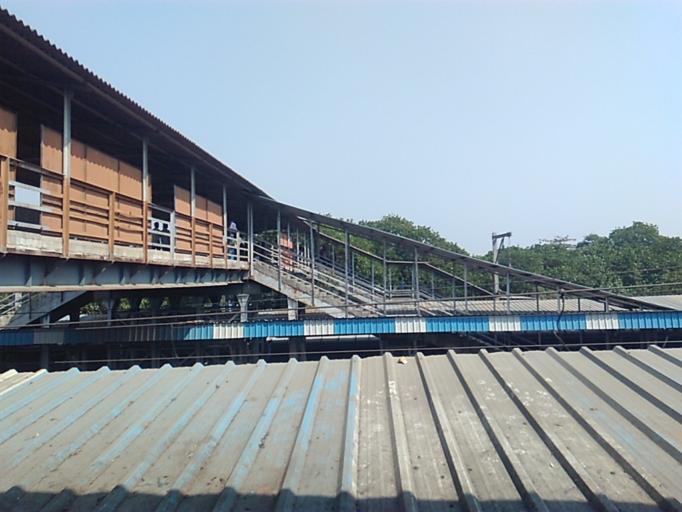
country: IN
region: Maharashtra
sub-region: Thane
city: Virar
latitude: 19.3826
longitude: 72.8321
